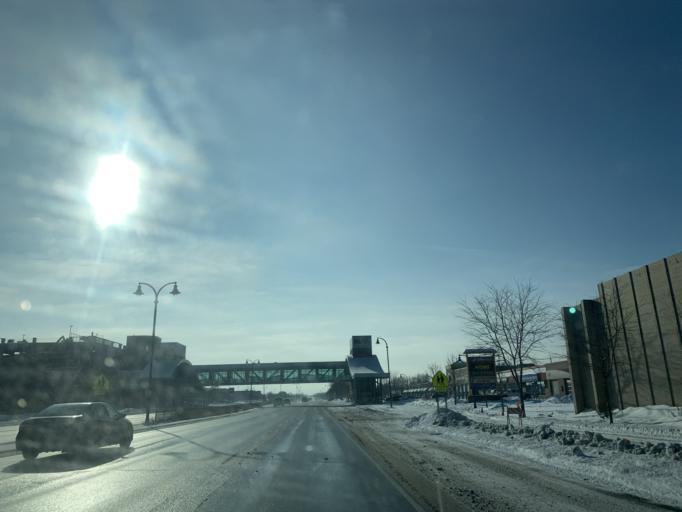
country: US
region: Minnesota
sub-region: Dakota County
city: Apple Valley
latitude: 44.7270
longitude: -93.2179
